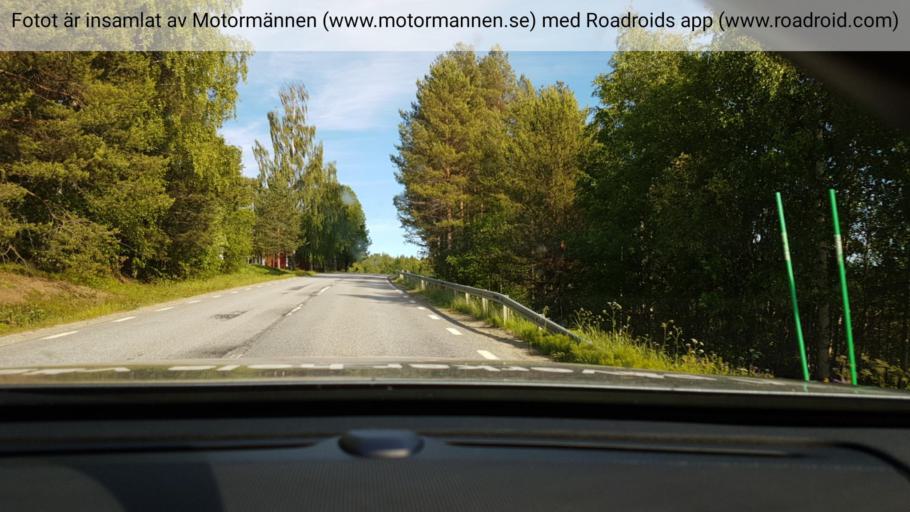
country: SE
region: Vaesterbotten
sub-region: Vindelns Kommun
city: Vindeln
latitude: 64.2783
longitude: 19.6262
